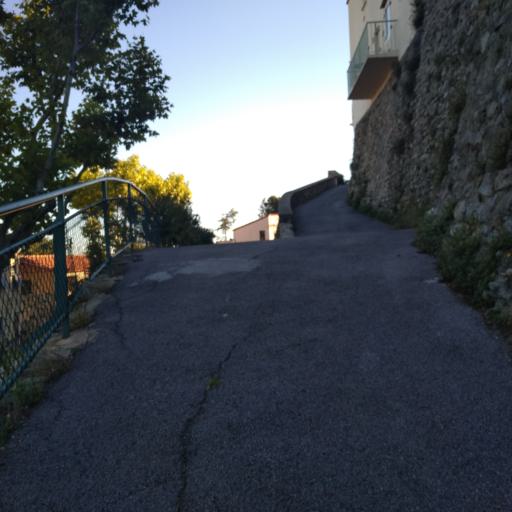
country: FR
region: Languedoc-Roussillon
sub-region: Departement des Pyrenees-Orientales
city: la Roca d'Albera
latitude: 42.5213
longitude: 2.9325
